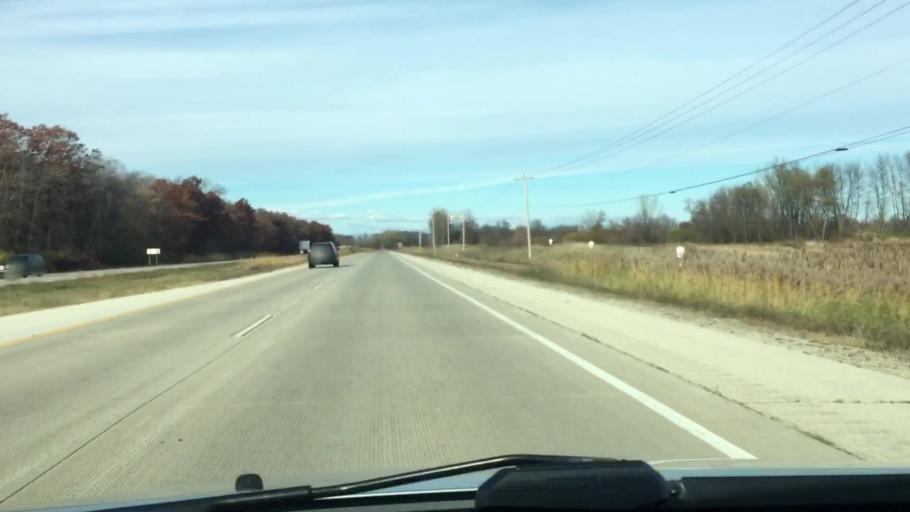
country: US
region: Wisconsin
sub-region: Brown County
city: Bellevue
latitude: 44.5535
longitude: -87.8812
